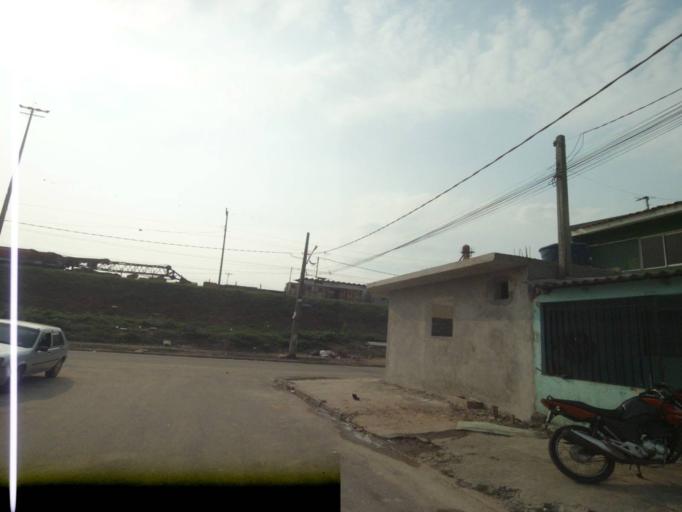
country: BR
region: Parana
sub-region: Sao Jose Dos Pinhais
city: Sao Jose dos Pinhais
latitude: -25.5348
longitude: -49.2317
